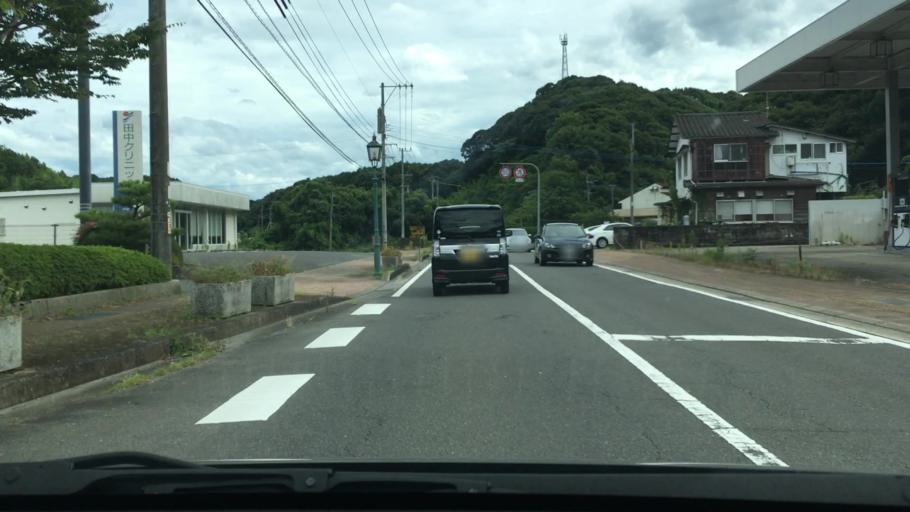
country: JP
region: Nagasaki
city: Sasebo
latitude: 32.9886
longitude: 129.7663
